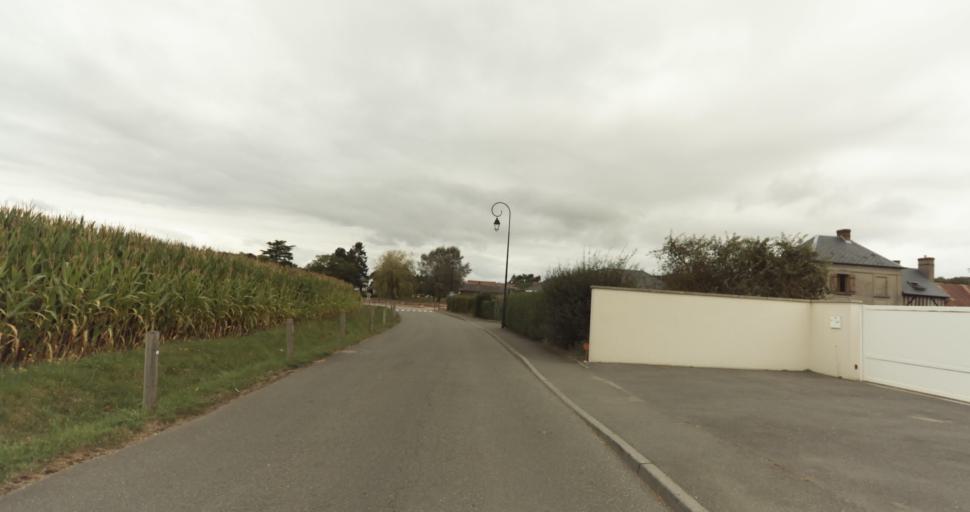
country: FR
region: Haute-Normandie
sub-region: Departement de l'Eure
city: Gravigny
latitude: 49.0295
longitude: 1.1968
